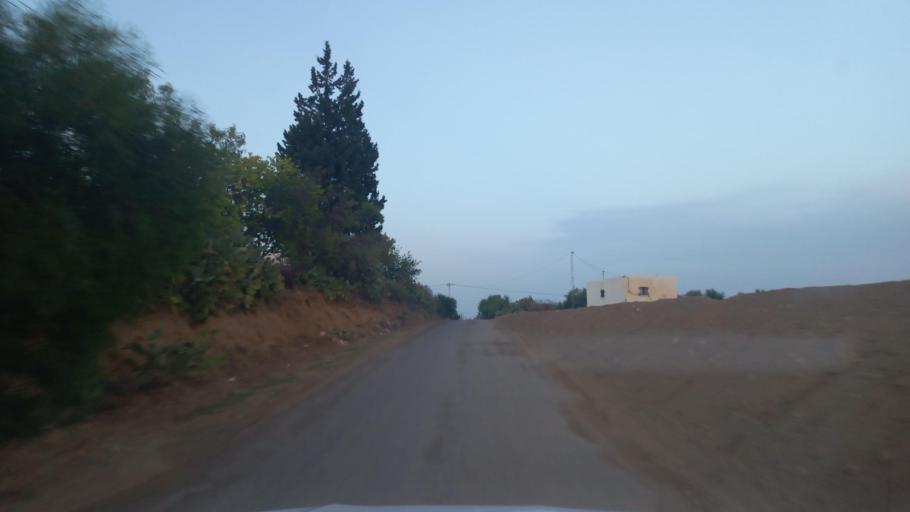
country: TN
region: Al Qasrayn
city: Kasserine
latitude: 35.2216
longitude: 9.0555
